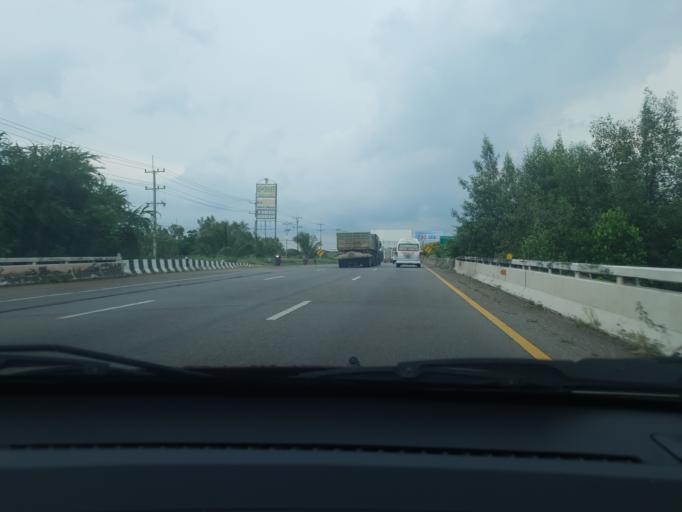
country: TH
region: Samut Sakhon
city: Ban Phaeo
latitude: 13.4800
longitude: 100.1188
